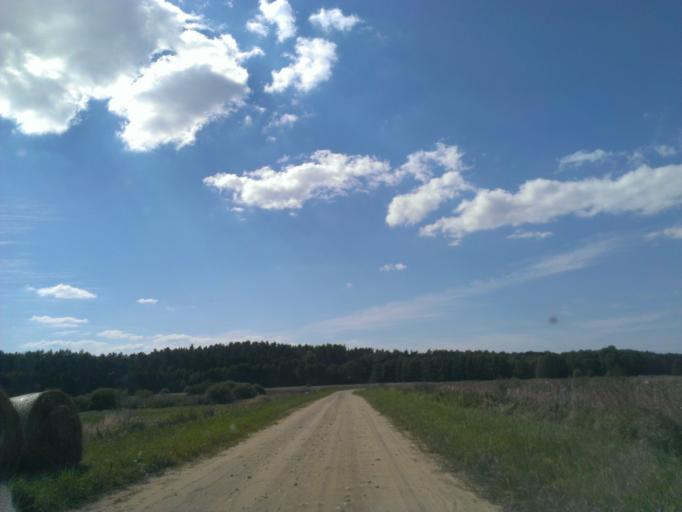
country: LV
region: Riga
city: Jaunciems
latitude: 57.0814
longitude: 24.2072
